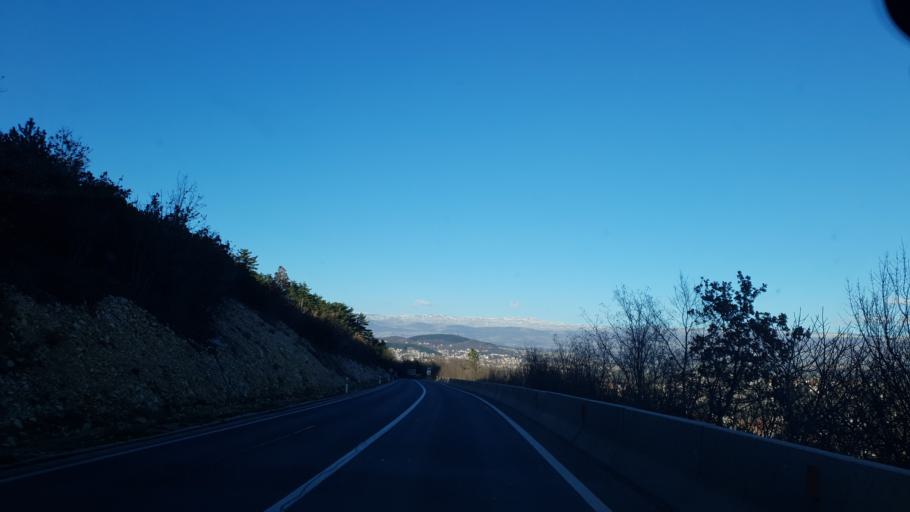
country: HR
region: Splitsko-Dalmatinska
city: Brnaze
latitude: 43.6681
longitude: 16.6493
